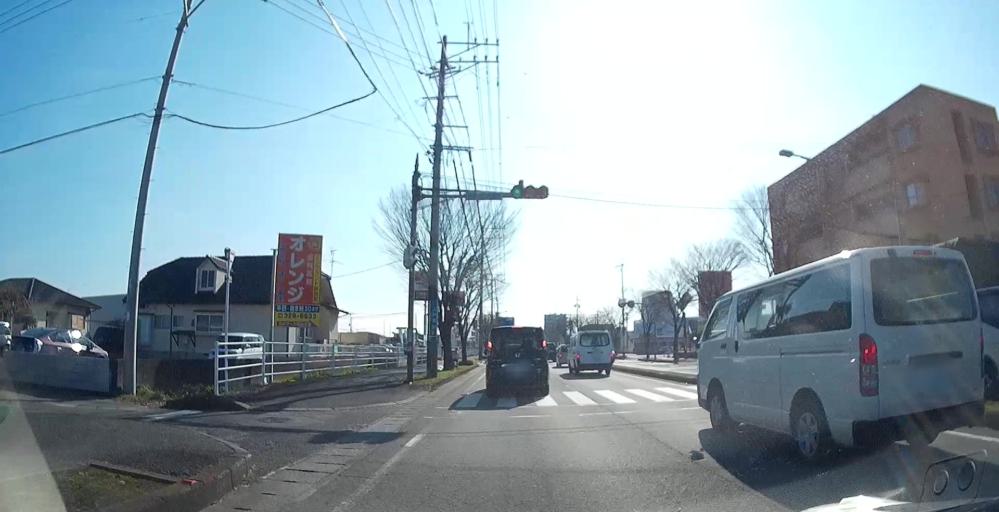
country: JP
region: Kumamoto
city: Kumamoto
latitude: 32.7776
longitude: 130.6731
